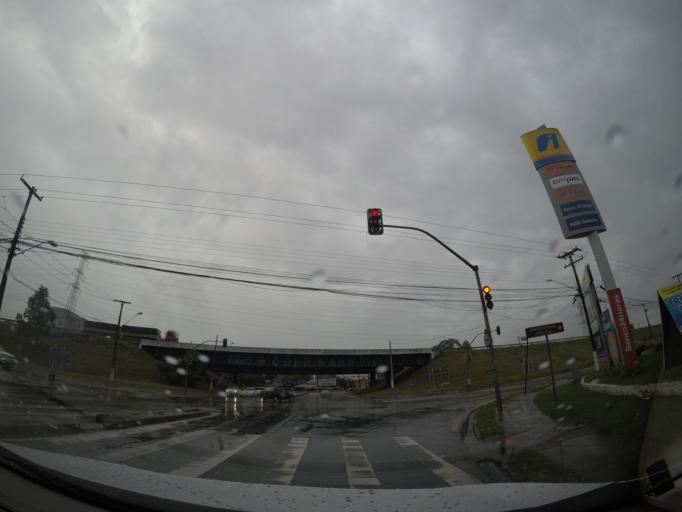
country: BR
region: Parana
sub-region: Curitiba
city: Curitiba
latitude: -25.4514
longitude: -49.3619
